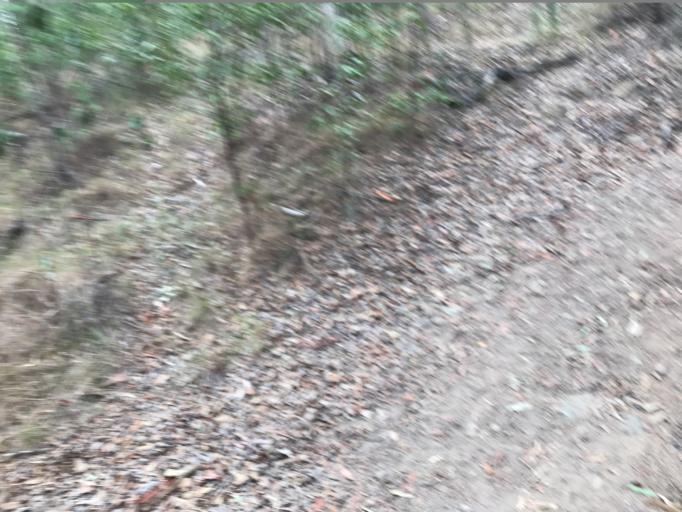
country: AU
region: Queensland
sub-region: Brisbane
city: Taringa
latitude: -27.4705
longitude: 152.9502
